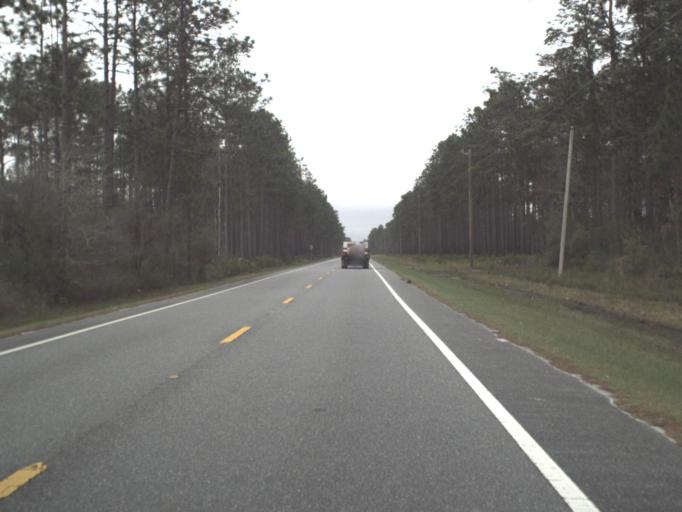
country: US
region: Florida
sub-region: Gulf County
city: Wewahitchka
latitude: 30.0073
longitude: -84.9783
